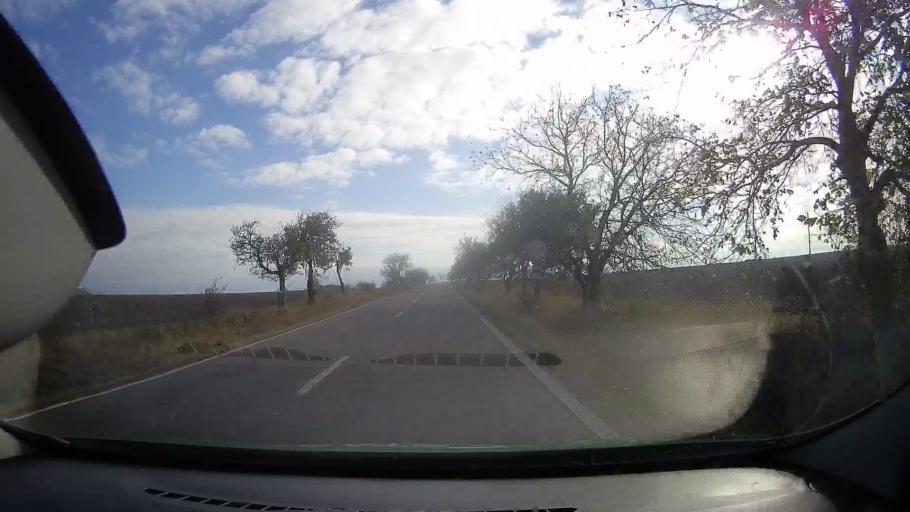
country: RO
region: Tulcea
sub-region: Comuna Bestepe
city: Bestepe
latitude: 45.0789
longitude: 29.0406
